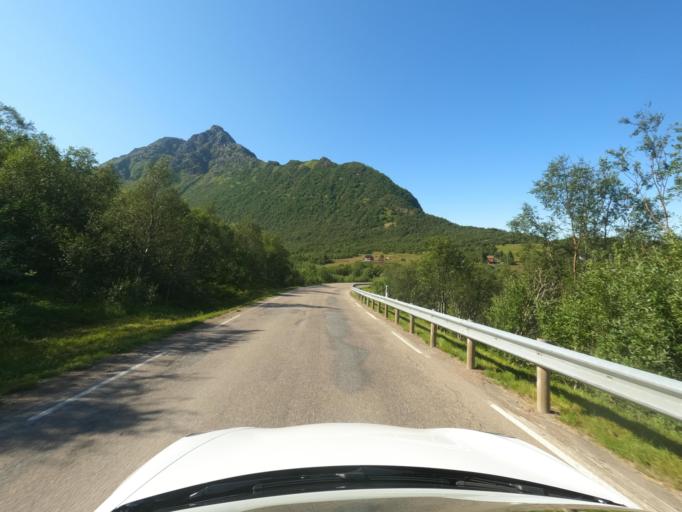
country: NO
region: Nordland
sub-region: Hadsel
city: Melbu
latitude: 68.4269
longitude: 14.8233
